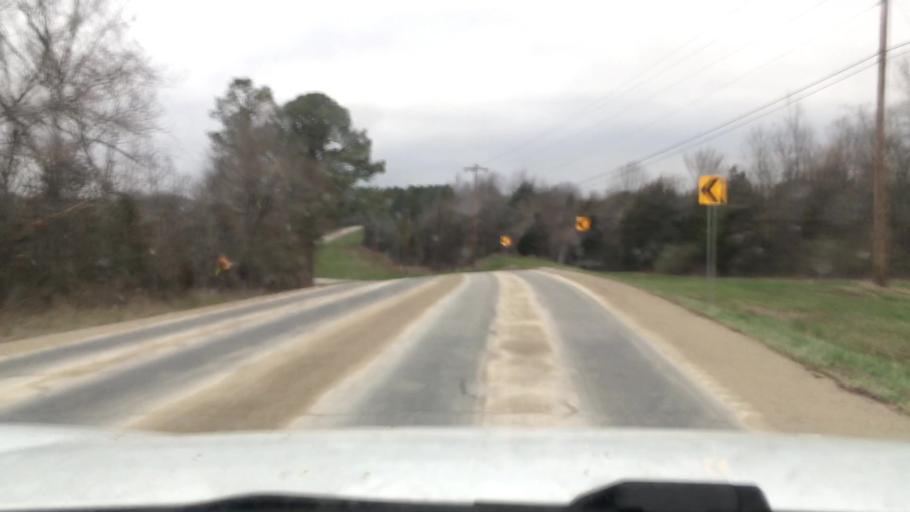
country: US
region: Missouri
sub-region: Saint Charles County
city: Weldon Spring
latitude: 38.6706
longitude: -90.7317
